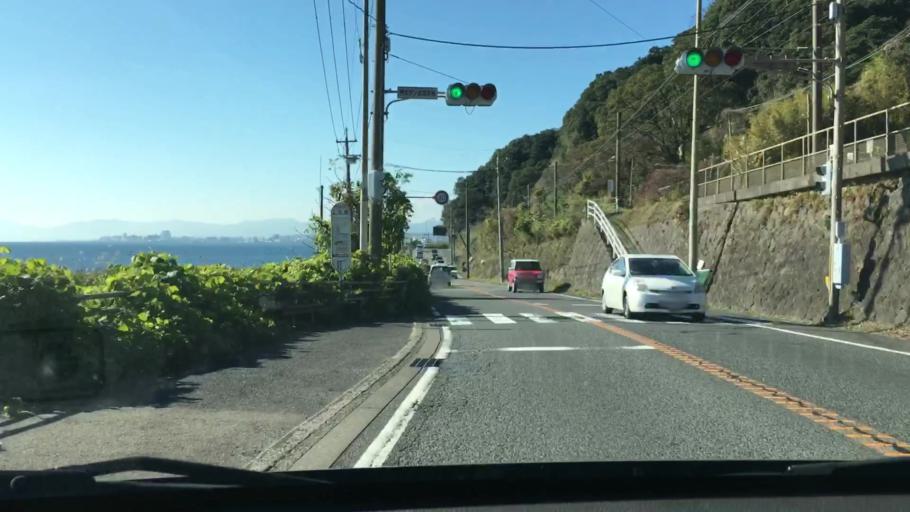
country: JP
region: Kagoshima
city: Kagoshima-shi
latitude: 31.6281
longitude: 130.5970
